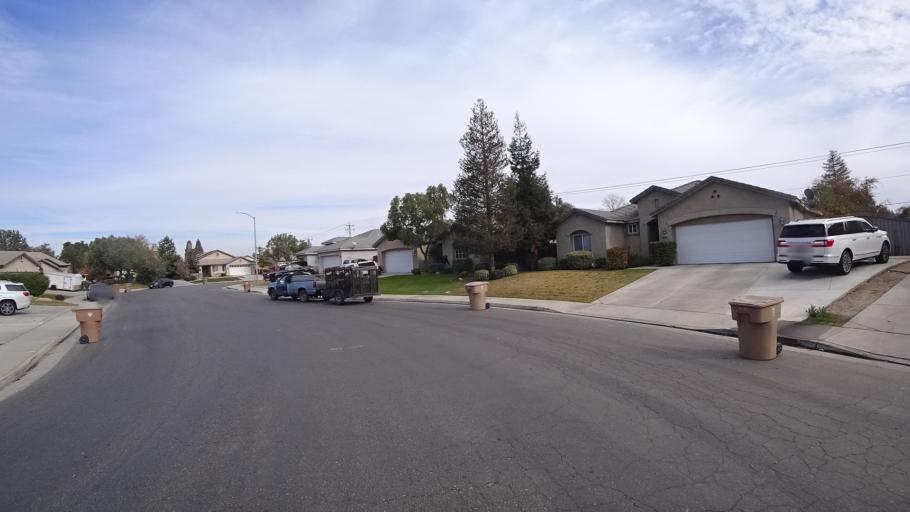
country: US
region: California
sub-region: Kern County
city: Rosedale
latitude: 35.3942
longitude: -119.1286
